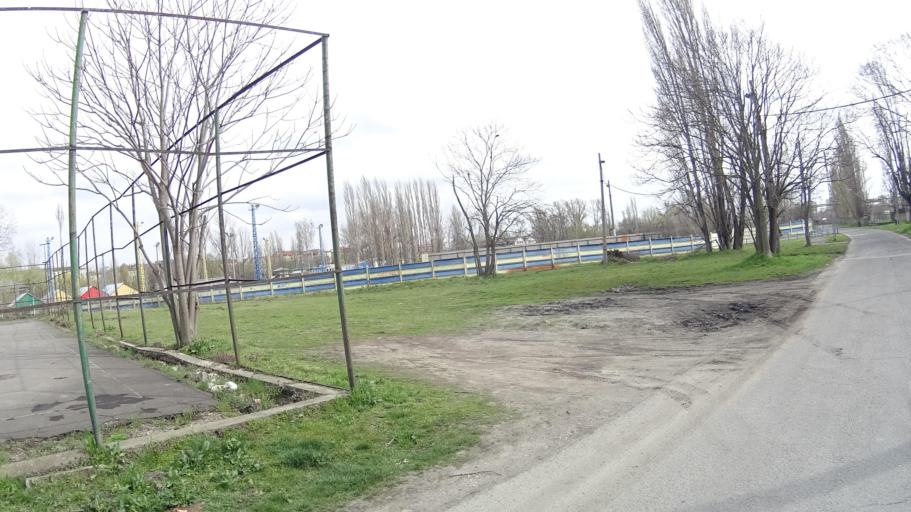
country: HU
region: Budapest
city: Budapest XXI. keruelet
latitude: 47.4343
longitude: 19.0858
